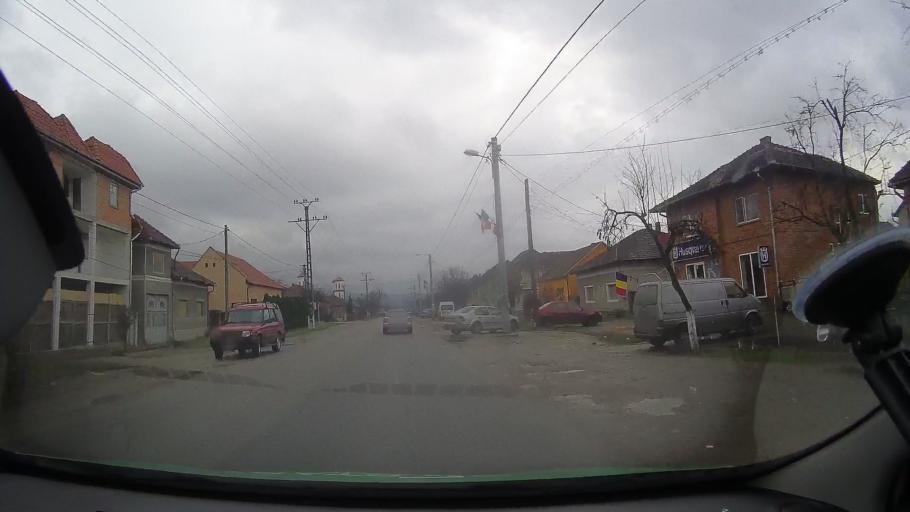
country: RO
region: Arad
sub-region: Comuna Sebis
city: Sebis
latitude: 46.3694
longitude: 22.1310
